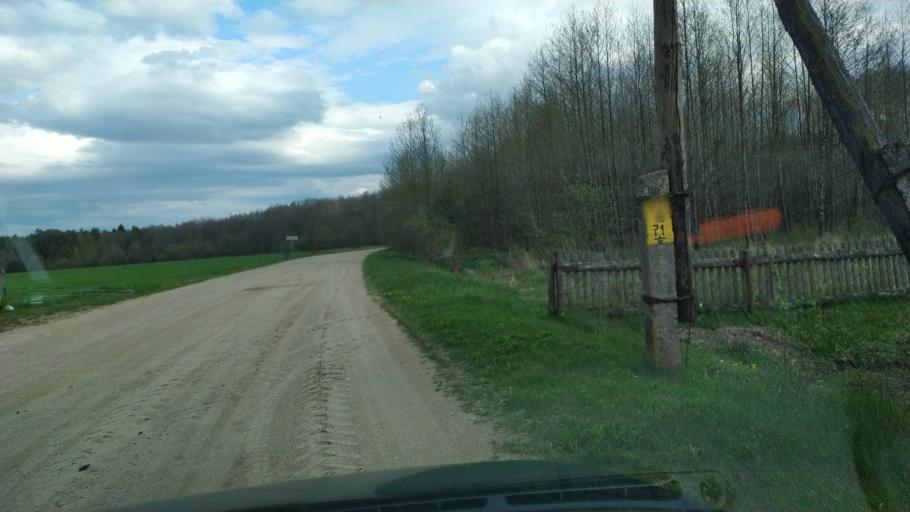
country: BY
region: Brest
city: Pruzhany
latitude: 52.7015
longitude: 24.2685
